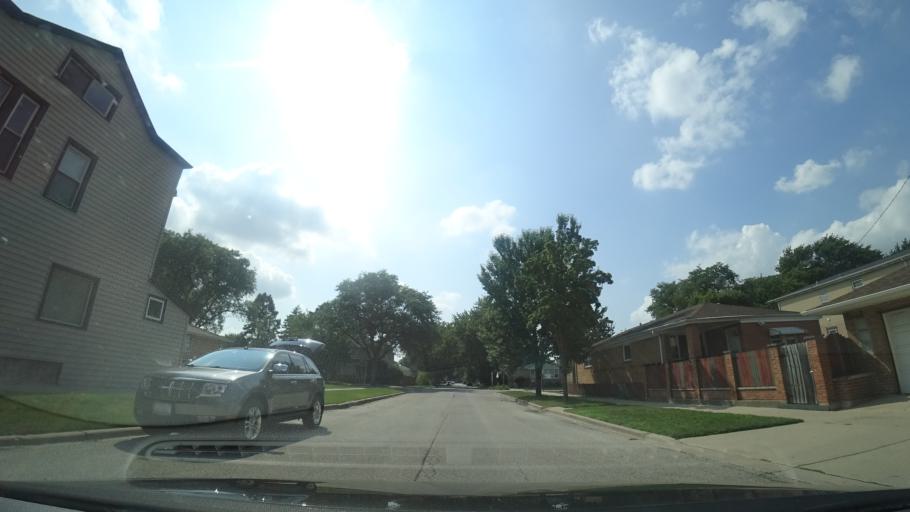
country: US
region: Illinois
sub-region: Cook County
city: Harwood Heights
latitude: 41.9712
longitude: -87.7791
